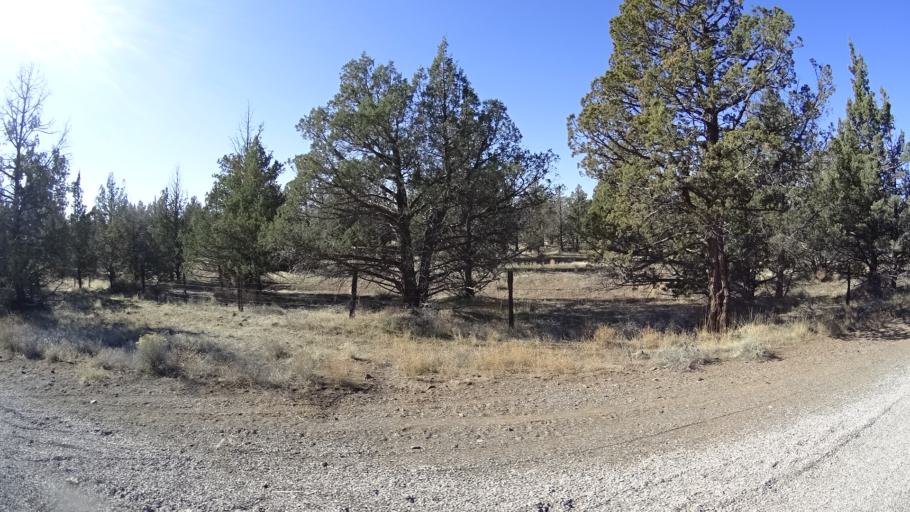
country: US
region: California
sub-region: Siskiyou County
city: Weed
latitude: 41.6111
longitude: -122.3125
